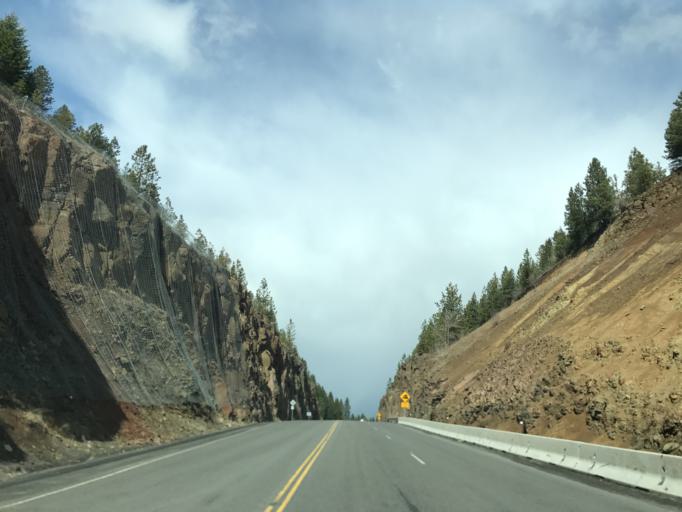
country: US
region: Idaho
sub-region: Idaho County
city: Grangeville
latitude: 45.8440
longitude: -116.2371
